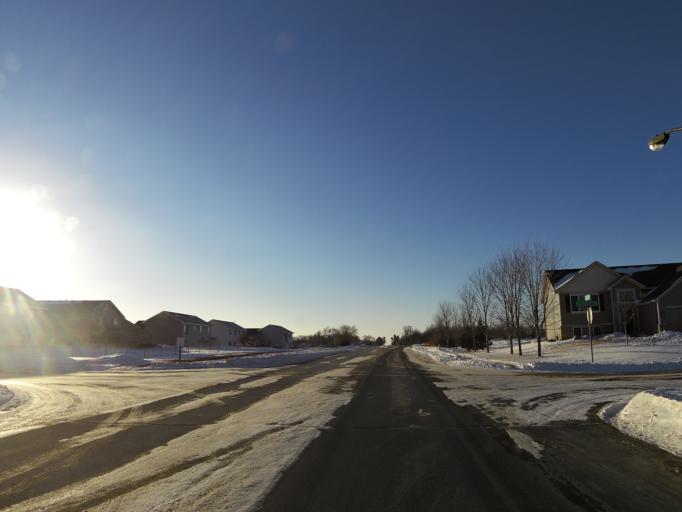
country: US
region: Minnesota
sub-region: Rice County
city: Lonsdale
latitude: 44.4864
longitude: -93.4202
